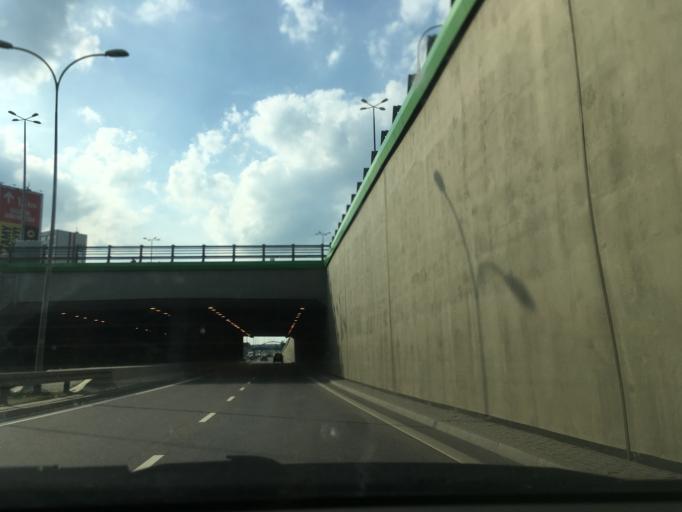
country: PL
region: Podlasie
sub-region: Bialystok
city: Bialystok
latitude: 53.1457
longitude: 23.1837
